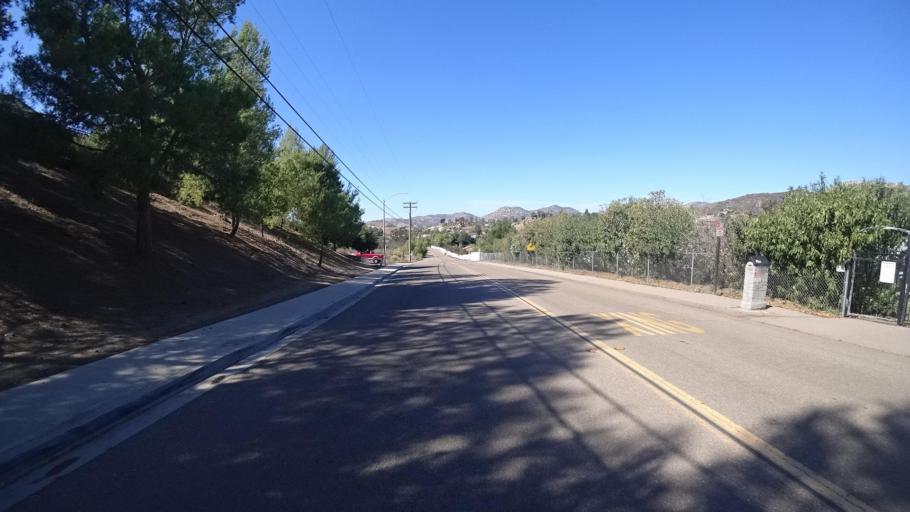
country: US
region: California
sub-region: San Diego County
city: Harbison Canyon
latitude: 32.8625
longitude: -116.8455
